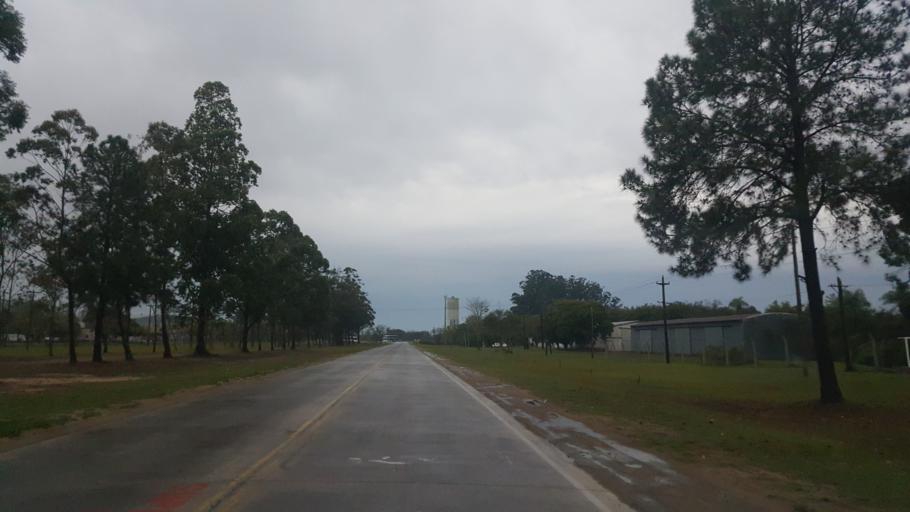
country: AR
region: Corrientes
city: Ituzaingo
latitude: -27.5820
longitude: -56.6763
